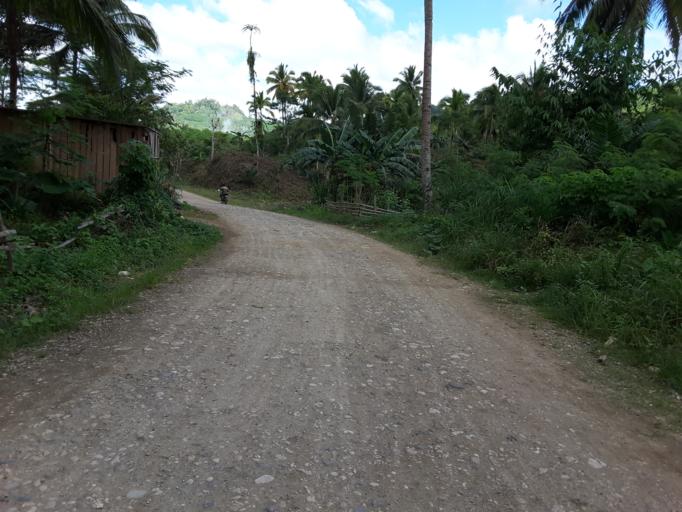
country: PH
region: Caraga
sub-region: Province of Agusan del Sur
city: Bayugan
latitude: 8.7197
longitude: 125.8417
